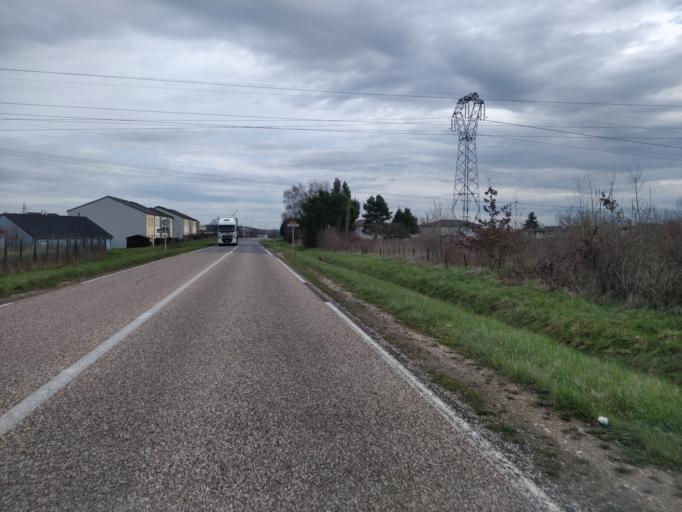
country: FR
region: Lorraine
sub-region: Departement de la Moselle
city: Uckange
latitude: 49.2957
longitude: 6.1406
